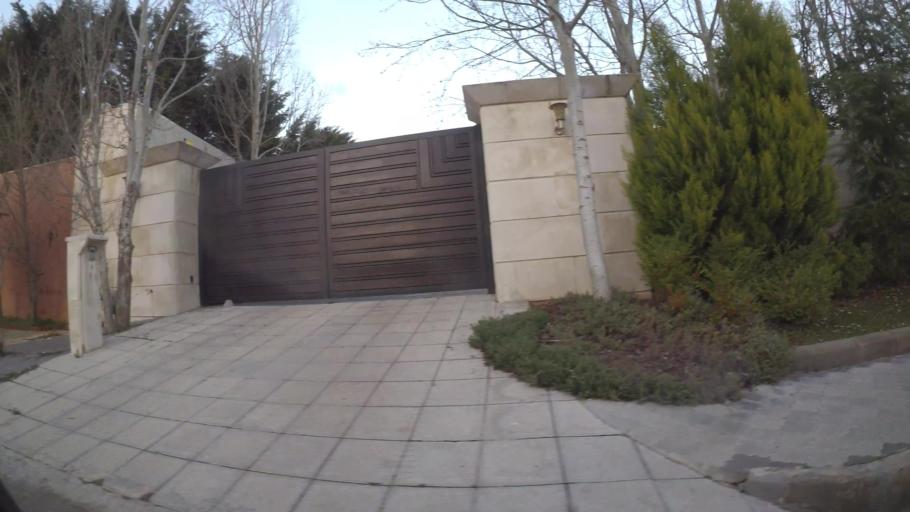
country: JO
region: Amman
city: Al Jubayhah
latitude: 32.0010
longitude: 35.8524
